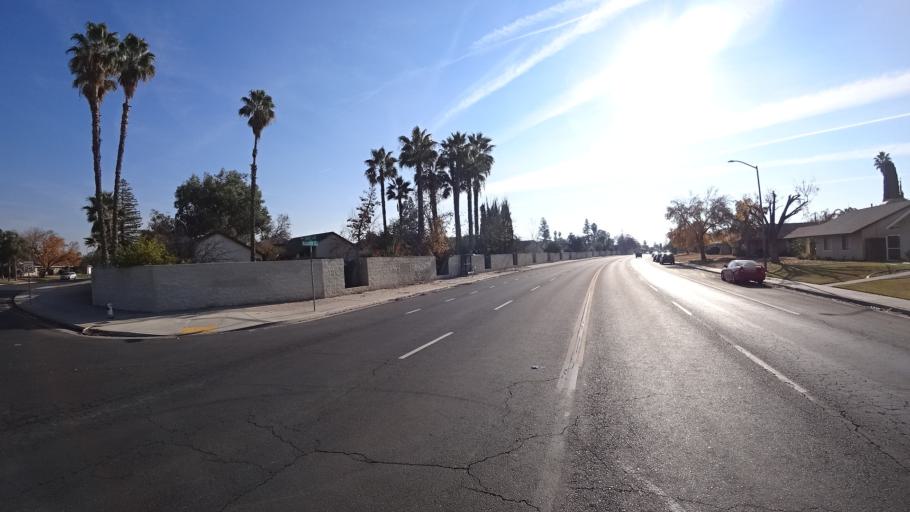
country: US
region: California
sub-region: Kern County
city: Bakersfield
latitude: 35.3232
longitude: -119.0661
